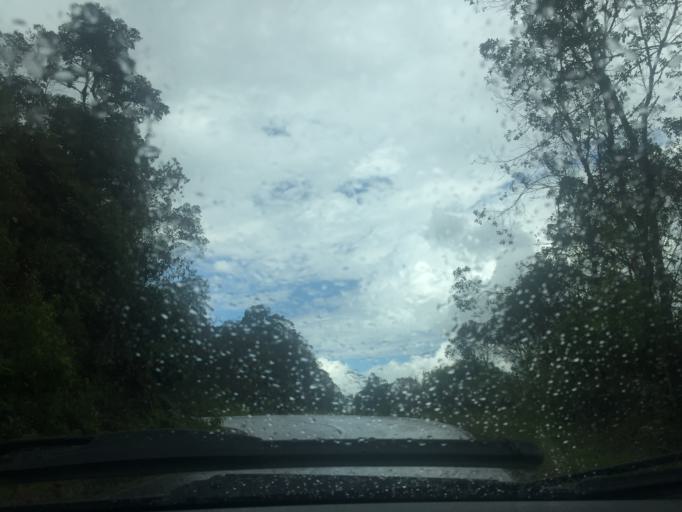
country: CO
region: Cundinamarca
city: Supata
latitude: 5.0315
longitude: -74.2469
